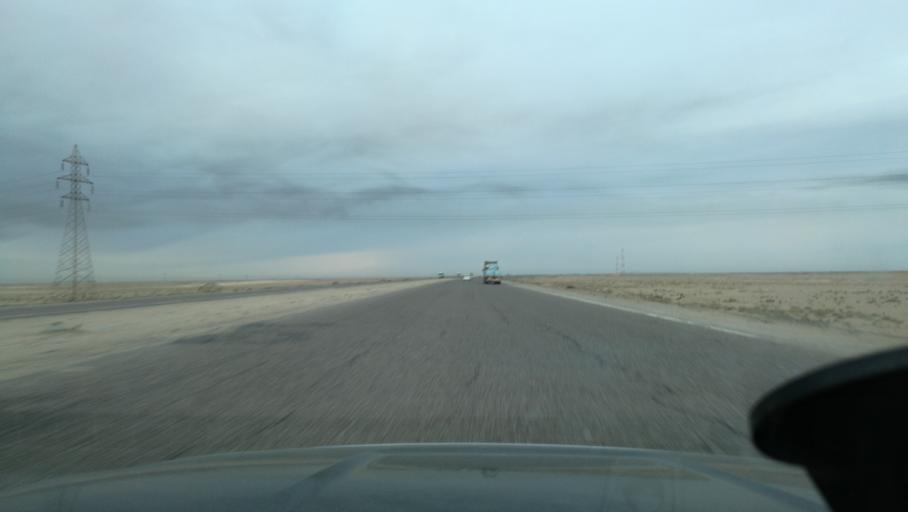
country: IQ
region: Basra Governorate
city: Az Zubayr
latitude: 30.4579
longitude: 47.3592
